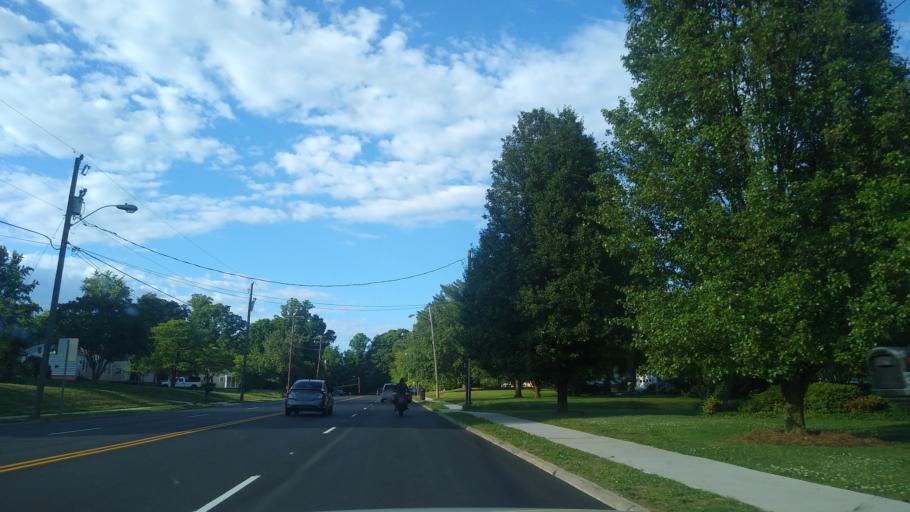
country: US
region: North Carolina
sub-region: Guilford County
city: Greensboro
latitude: 36.1191
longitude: -79.7740
